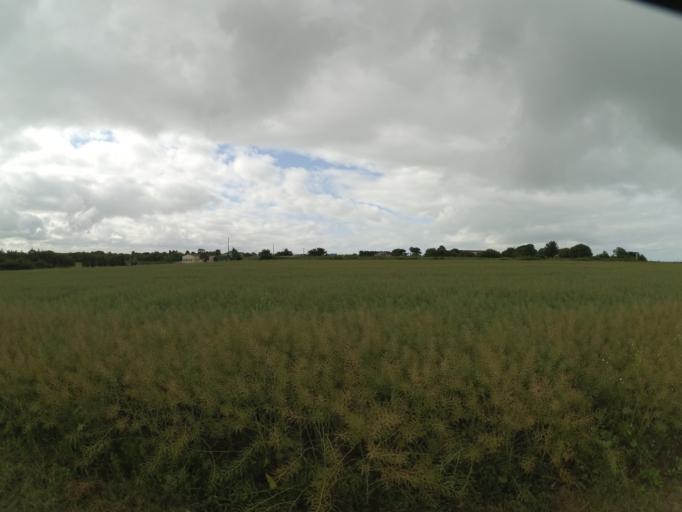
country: FR
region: Poitou-Charentes
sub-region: Departement de la Charente-Maritime
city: Aytre
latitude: 46.1314
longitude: -1.1325
